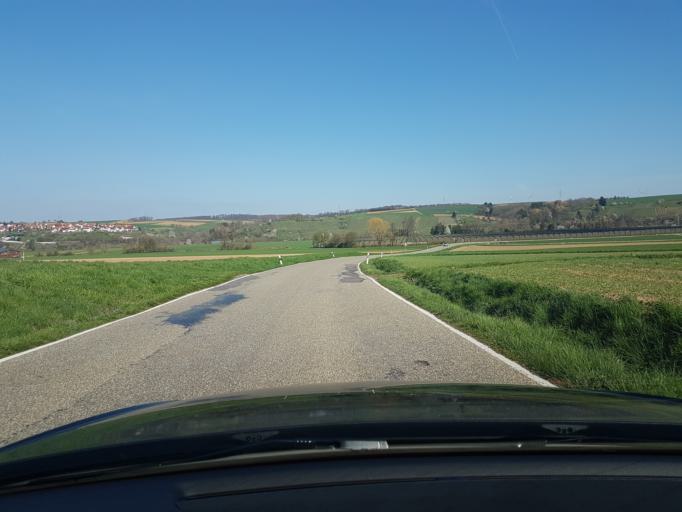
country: DE
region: Baden-Wuerttemberg
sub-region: Regierungsbezirk Stuttgart
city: Neuenstadt am Kocher
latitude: 49.2356
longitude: 9.3822
